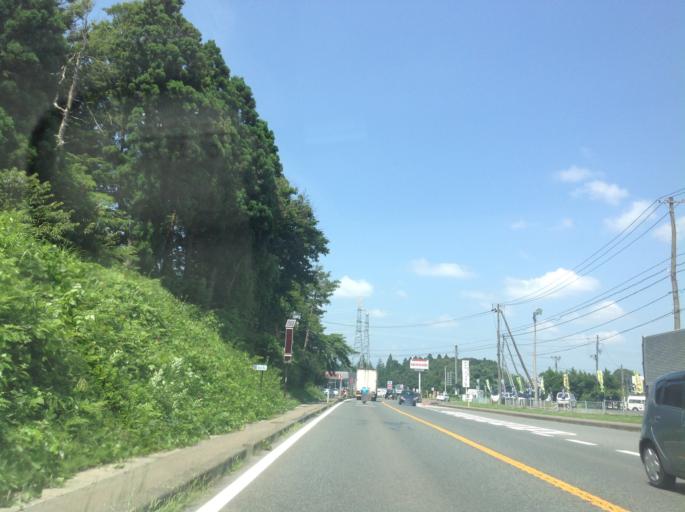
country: JP
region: Iwate
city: Hanamaki
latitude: 39.3435
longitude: 141.1072
